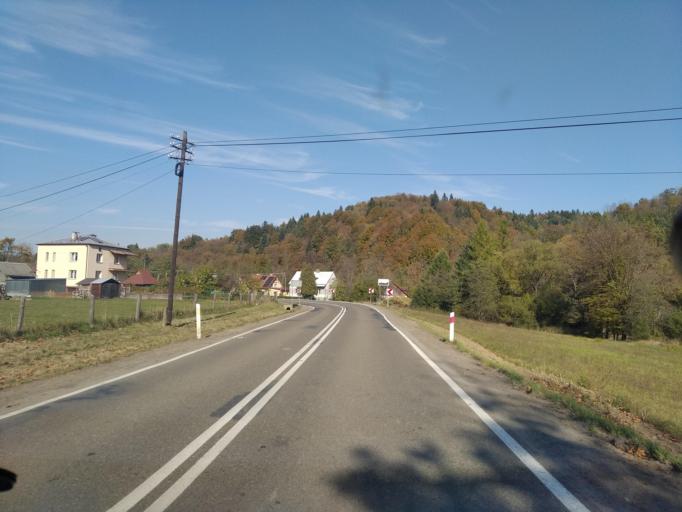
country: PL
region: Subcarpathian Voivodeship
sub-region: Powiat leski
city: Baligrod
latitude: 49.3866
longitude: 22.2874
